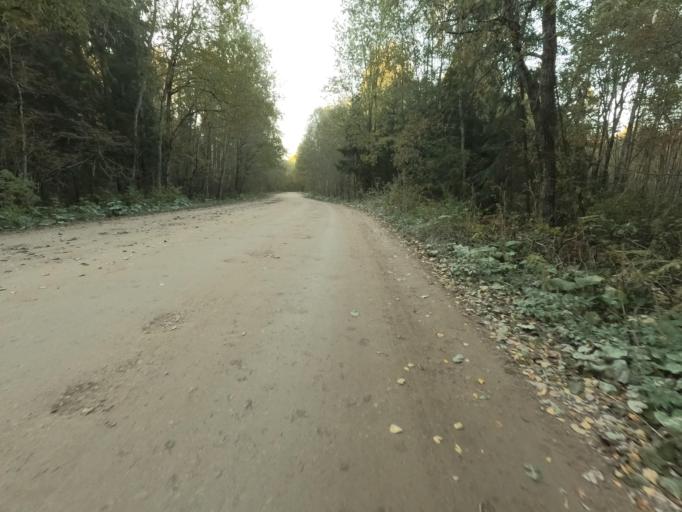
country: RU
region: Leningrad
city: Lyuban'
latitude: 59.0053
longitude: 31.0950
